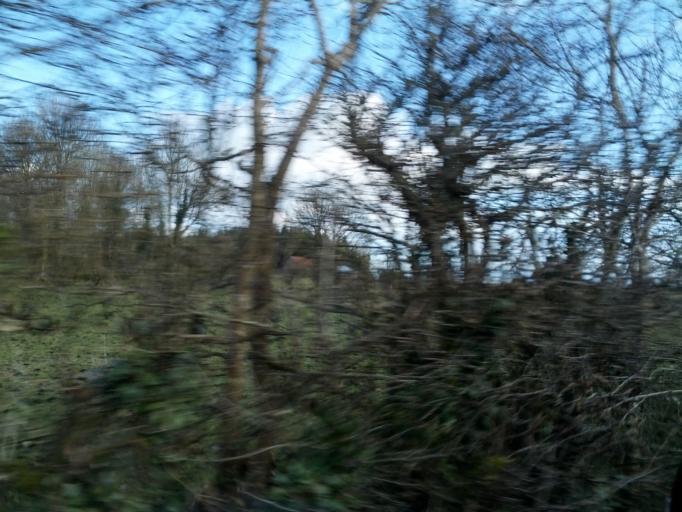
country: IE
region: Connaught
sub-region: County Galway
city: Athenry
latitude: 53.3907
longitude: -8.6228
